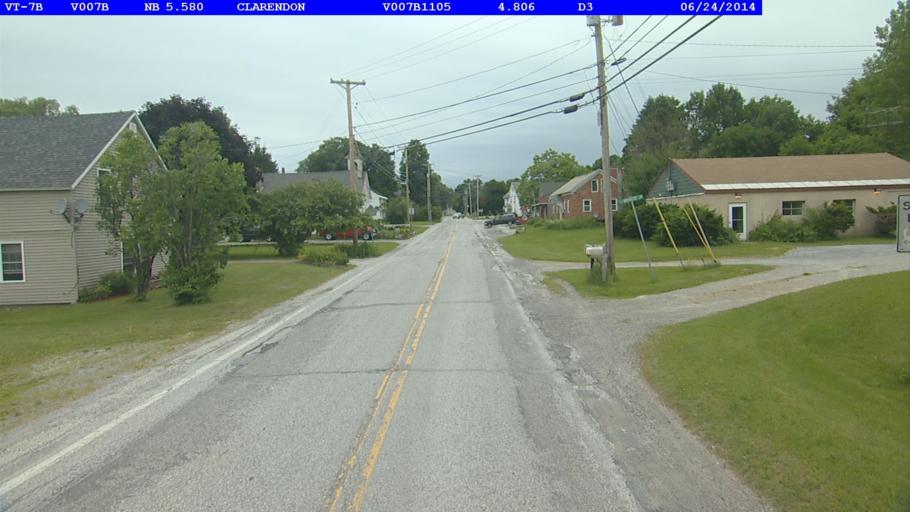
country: US
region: Vermont
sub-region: Rutland County
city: Rutland
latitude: 43.5657
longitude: -72.9659
